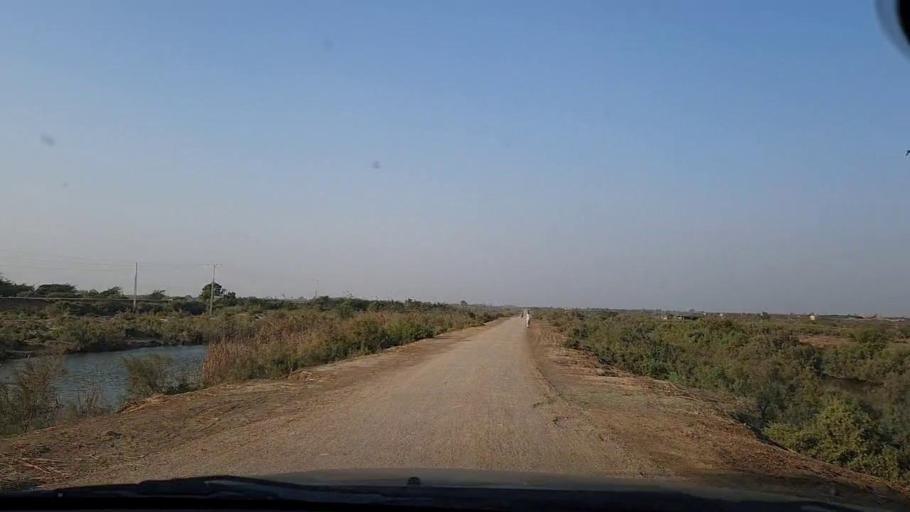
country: PK
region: Sindh
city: Chuhar Jamali
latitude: 24.3069
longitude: 67.7555
